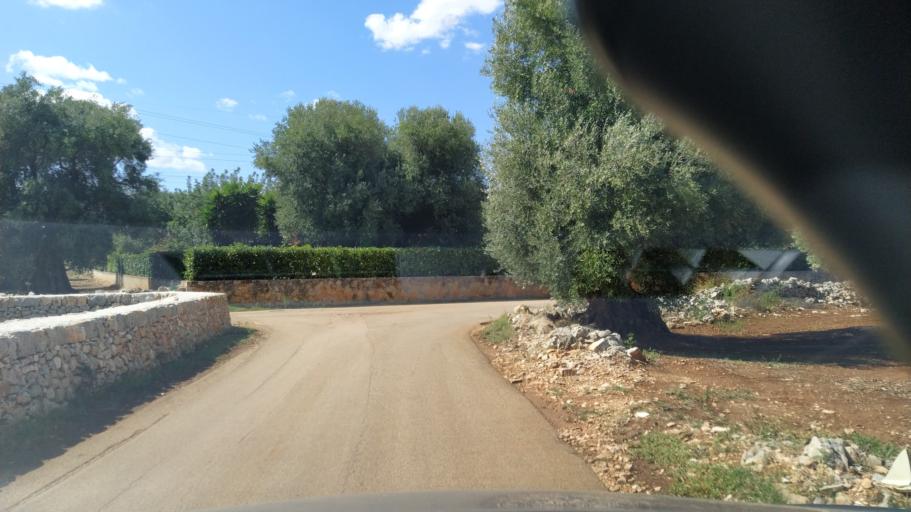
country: IT
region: Apulia
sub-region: Provincia di Brindisi
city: Fasano
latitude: 40.8240
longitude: 17.3656
